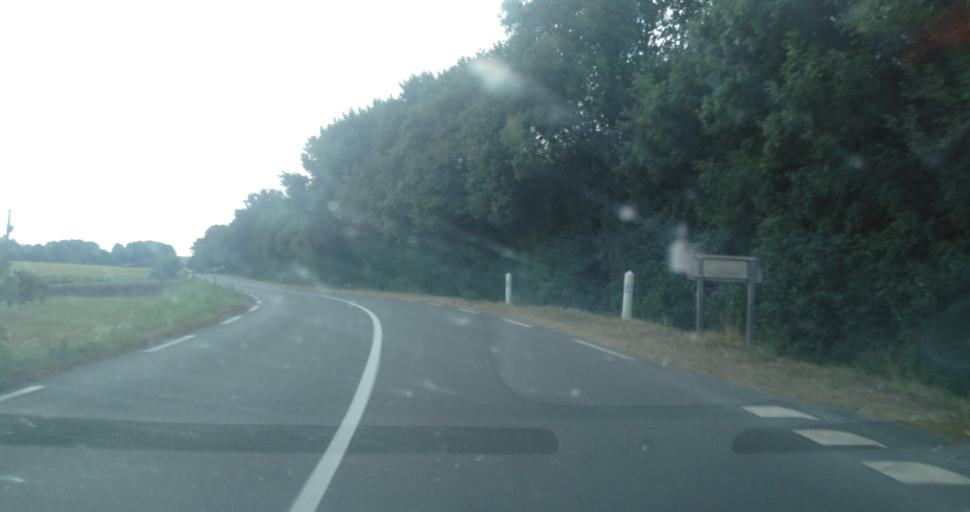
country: FR
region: Pays de la Loire
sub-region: Departement de la Vendee
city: Sainte-Hermine
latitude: 46.5858
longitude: -1.1167
